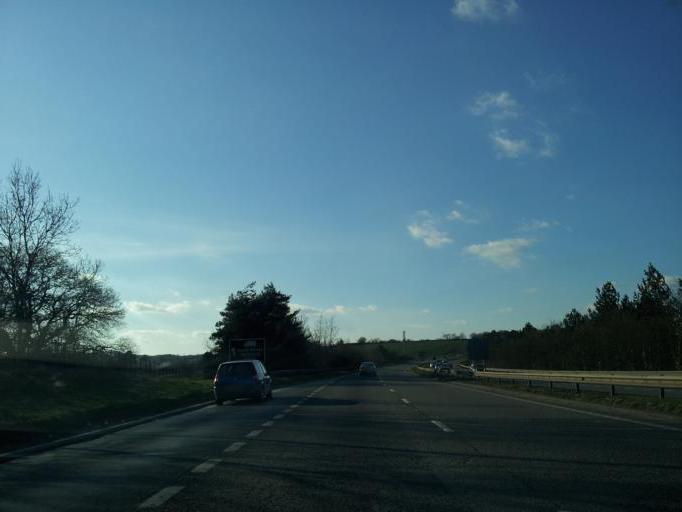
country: GB
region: England
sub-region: Devon
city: Exeter
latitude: 50.6886
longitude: -3.5328
